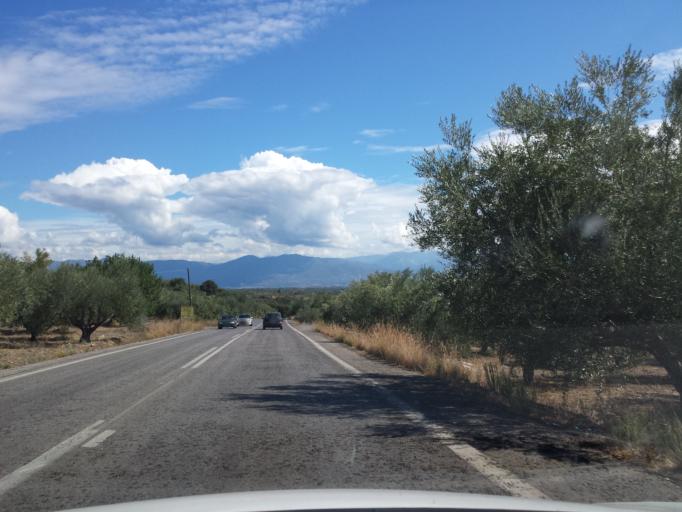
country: GR
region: Peloponnese
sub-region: Nomos Messinias
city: Messini
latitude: 37.0070
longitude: 21.9082
